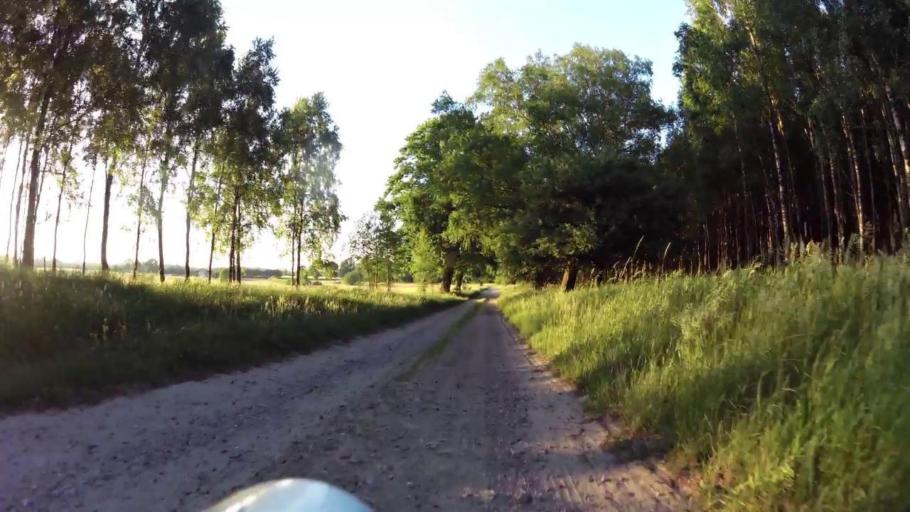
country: PL
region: West Pomeranian Voivodeship
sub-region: Powiat szczecinecki
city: Szczecinek
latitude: 53.8398
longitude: 16.6898
